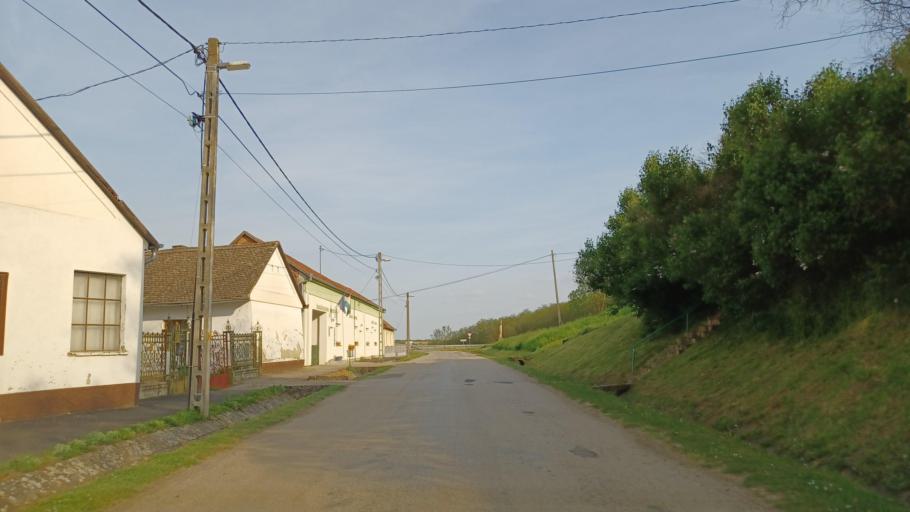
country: HU
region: Baranya
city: Villany
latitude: 45.9561
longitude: 18.3860
